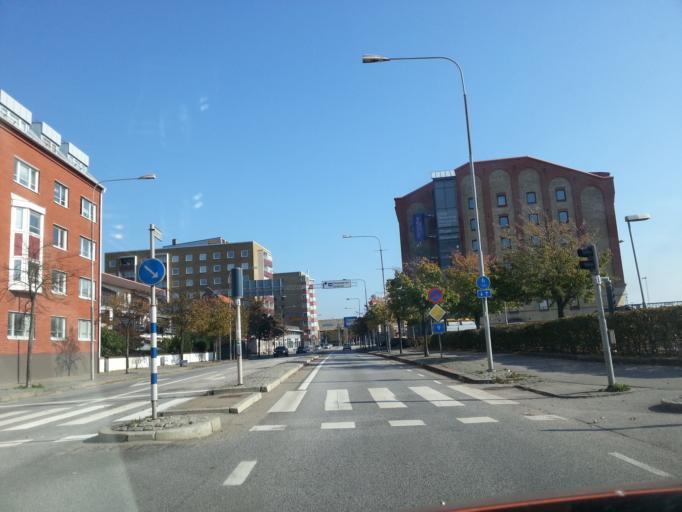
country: SE
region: Skane
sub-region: Trelleborgs Kommun
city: Trelleborg
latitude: 55.3733
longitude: 13.1526
